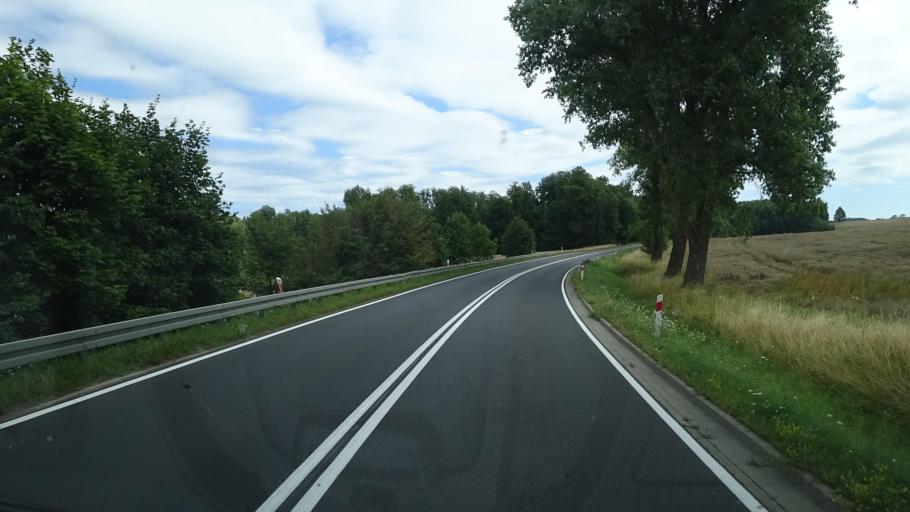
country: PL
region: Warmian-Masurian Voivodeship
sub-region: Powiat elcki
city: Stare Juchy
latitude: 53.7947
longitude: 22.2157
